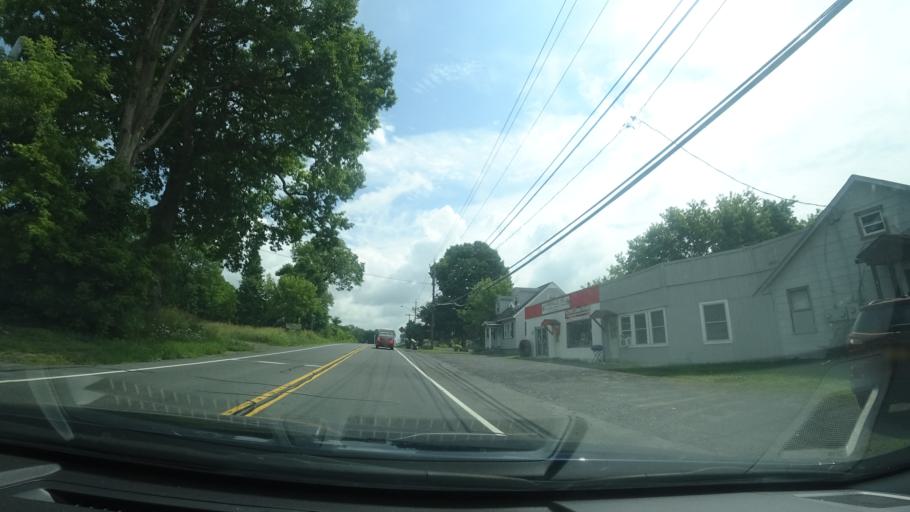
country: US
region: New York
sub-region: Washington County
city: Hudson Falls
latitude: 43.3156
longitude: -73.6053
